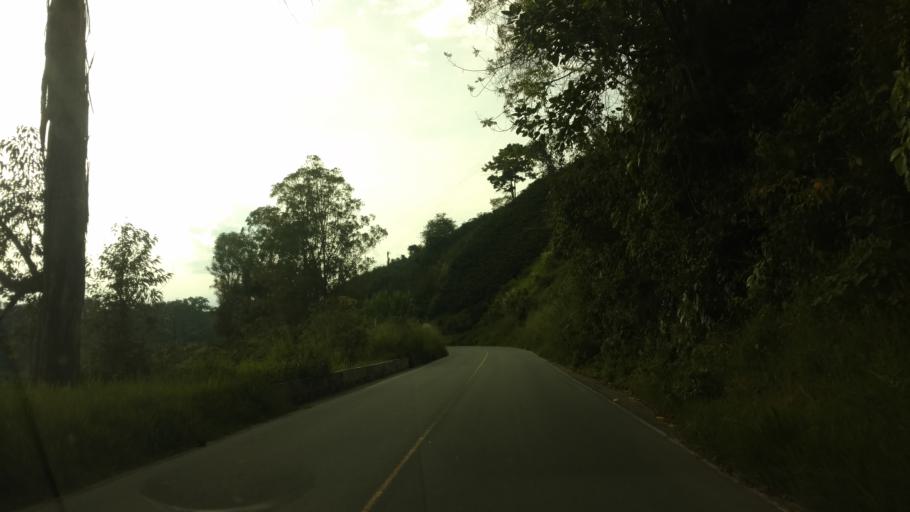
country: CO
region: Caldas
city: Neira
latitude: 5.1863
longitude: -75.5446
